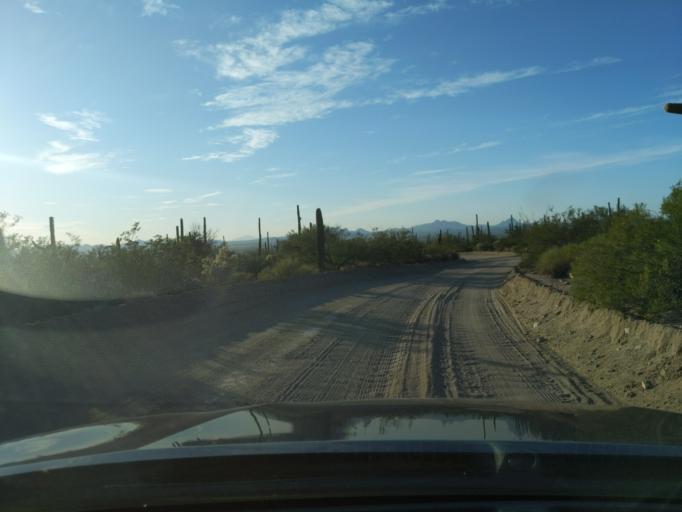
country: US
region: Arizona
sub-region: Pima County
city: Picture Rocks
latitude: 32.2879
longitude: -111.1963
